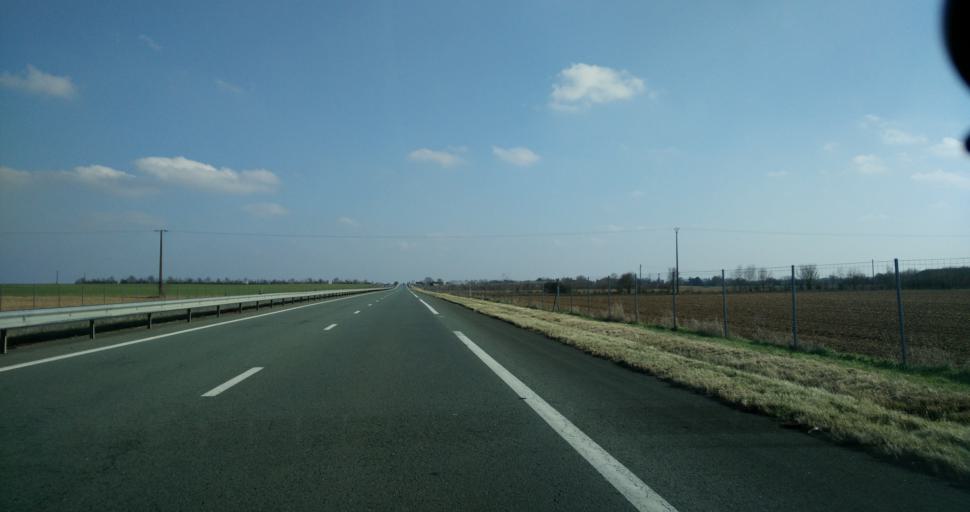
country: FR
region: Poitou-Charentes
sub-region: Departement des Deux-Sevres
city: Mauze-sur-le-Mignon
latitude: 46.2007
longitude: -0.7109
